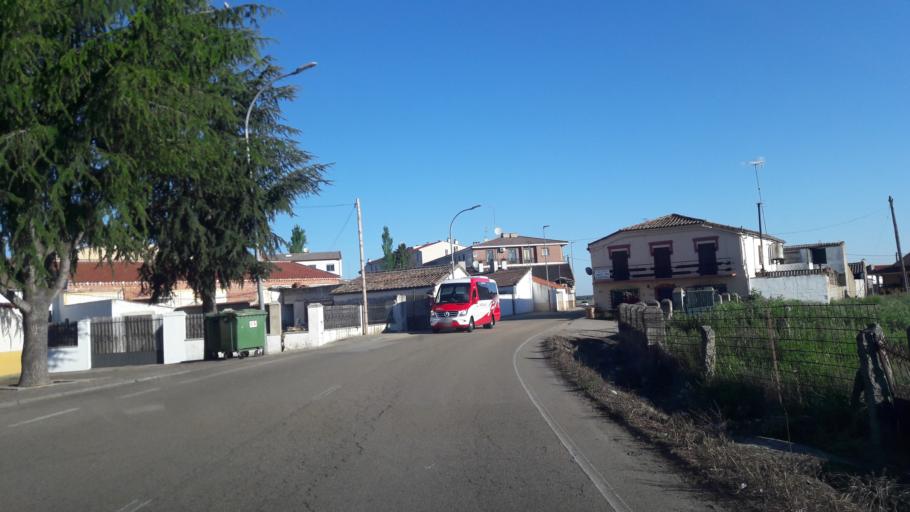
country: ES
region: Castille and Leon
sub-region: Provincia de Salamanca
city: La Fuente de San Esteban
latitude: 40.8022
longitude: -6.2551
